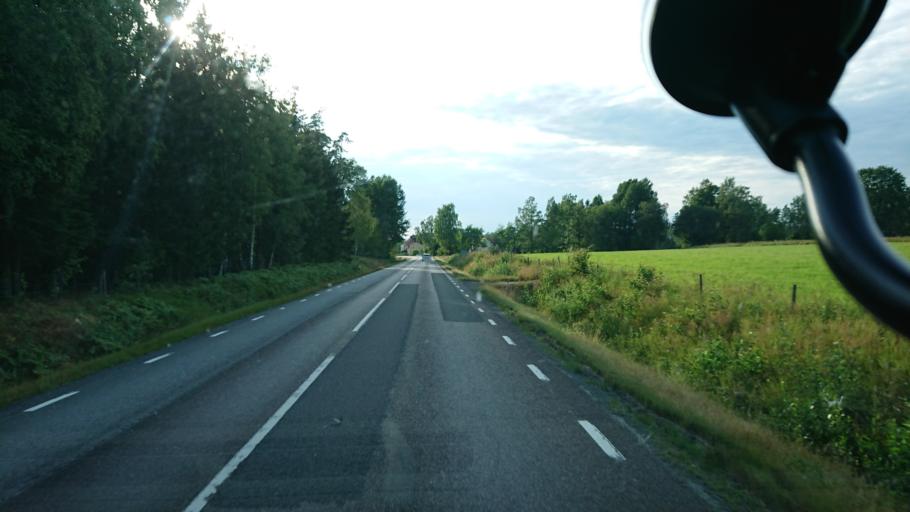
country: SE
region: Kronoberg
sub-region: Vaxjo Kommun
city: Braas
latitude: 57.0196
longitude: 15.0422
